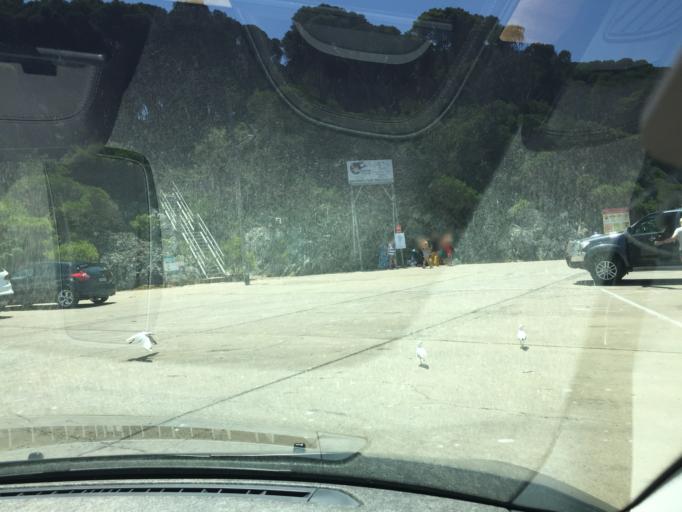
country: AU
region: New South Wales
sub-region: Bega Valley
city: Bega
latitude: -36.7369
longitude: 149.9827
